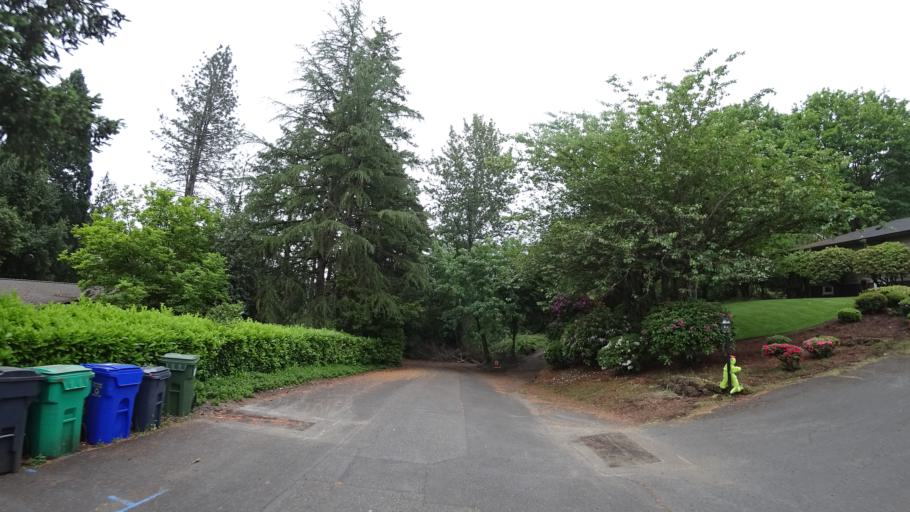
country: US
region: Oregon
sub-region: Clackamas County
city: Lake Oswego
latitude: 45.4370
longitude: -122.7064
